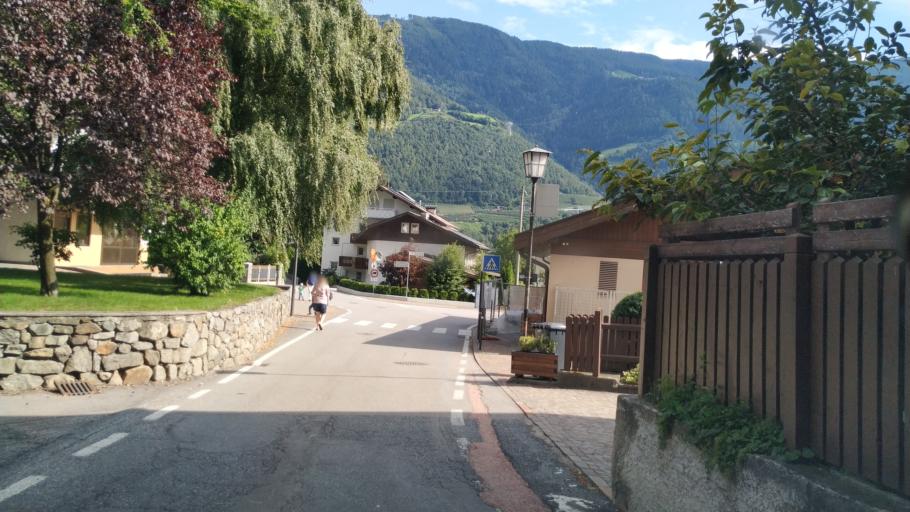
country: IT
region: Trentino-Alto Adige
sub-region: Bolzano
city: Rabla
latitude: 46.6719
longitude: 11.0610
